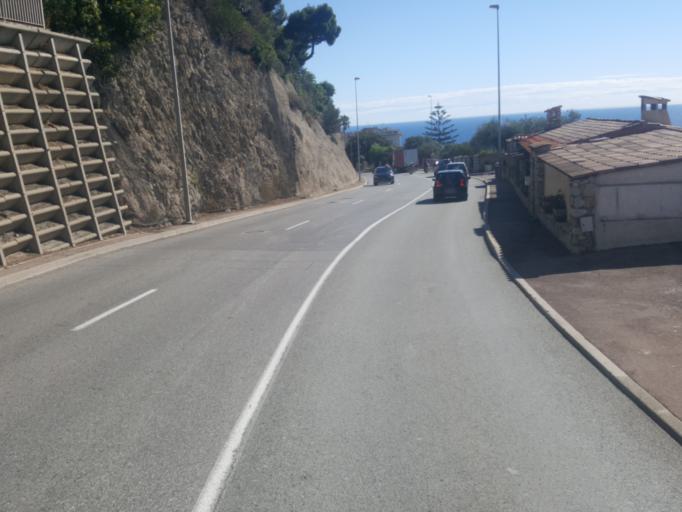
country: FR
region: Provence-Alpes-Cote d'Azur
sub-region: Departement des Alpes-Maritimes
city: Cap-d'Ail
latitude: 43.7244
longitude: 7.4032
